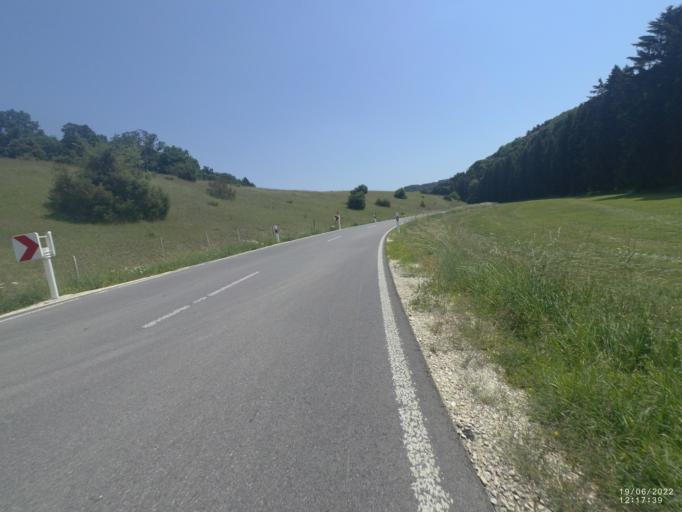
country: DE
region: Baden-Wuerttemberg
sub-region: Regierungsbezirk Stuttgart
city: Gerstetten
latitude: 48.6079
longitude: 9.9890
